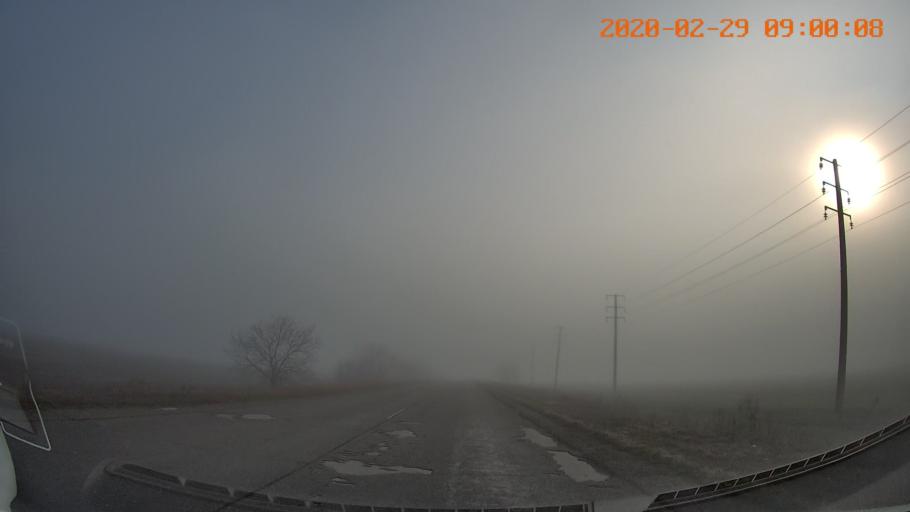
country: MD
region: Telenesti
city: Tiraspolul Nou
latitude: 46.9216
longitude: 29.6707
